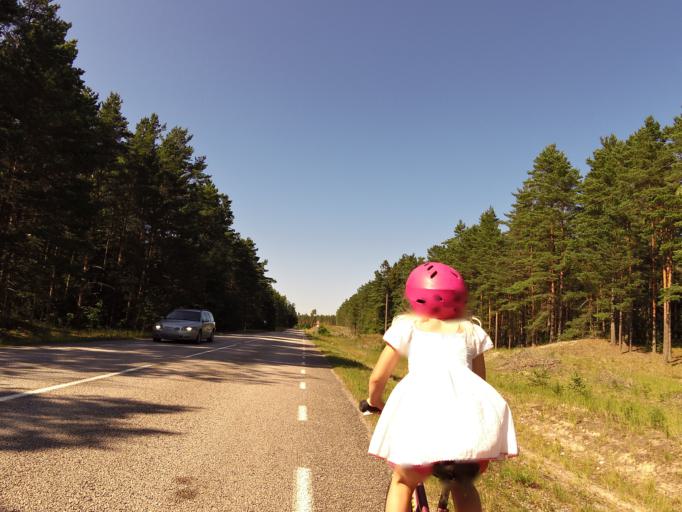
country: EE
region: Hiiumaa
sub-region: Kaerdla linn
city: Kardla
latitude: 58.8509
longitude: 22.4651
